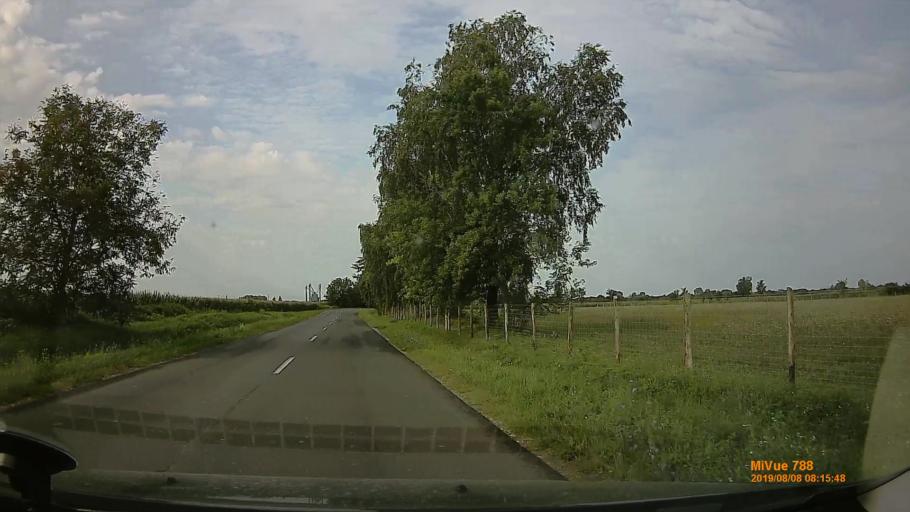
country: HR
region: Medimurska
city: Kotoriba
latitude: 46.3942
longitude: 16.8417
